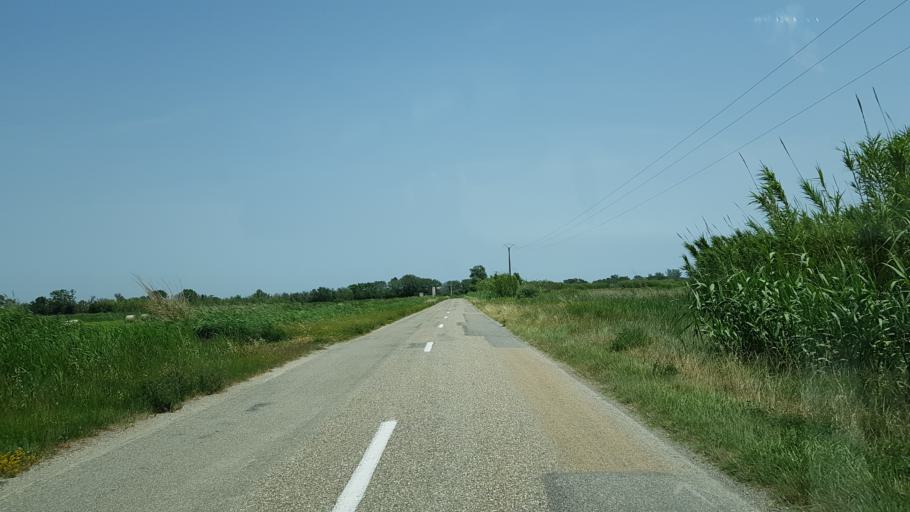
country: FR
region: Provence-Alpes-Cote d'Azur
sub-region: Departement des Bouches-du-Rhone
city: Port-Saint-Louis-du-Rhone
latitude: 43.4444
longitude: 4.6702
